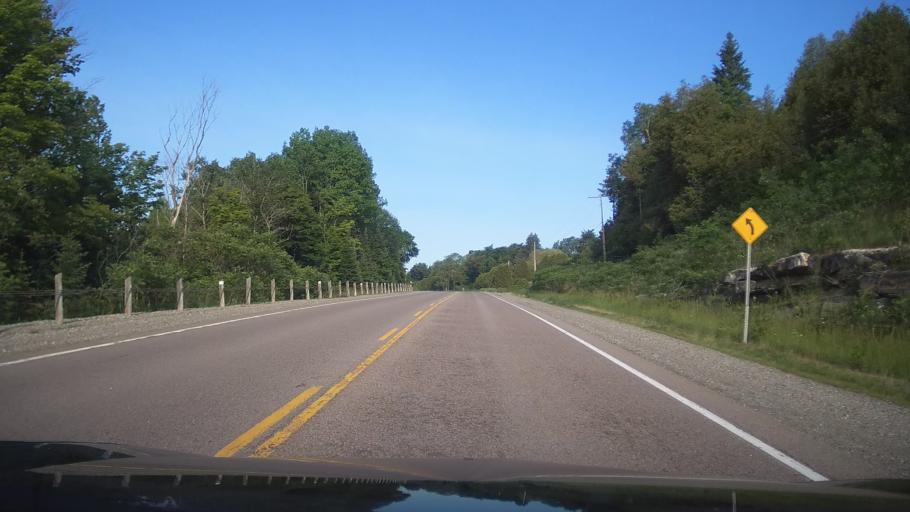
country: CA
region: Ontario
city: Skatepark
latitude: 44.7542
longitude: -76.8746
